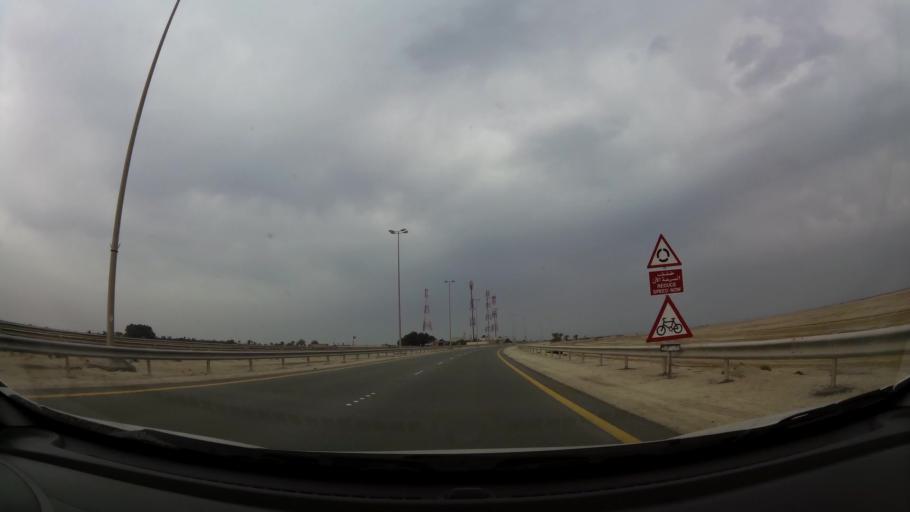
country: BH
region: Central Governorate
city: Dar Kulayb
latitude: 25.9937
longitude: 50.4719
